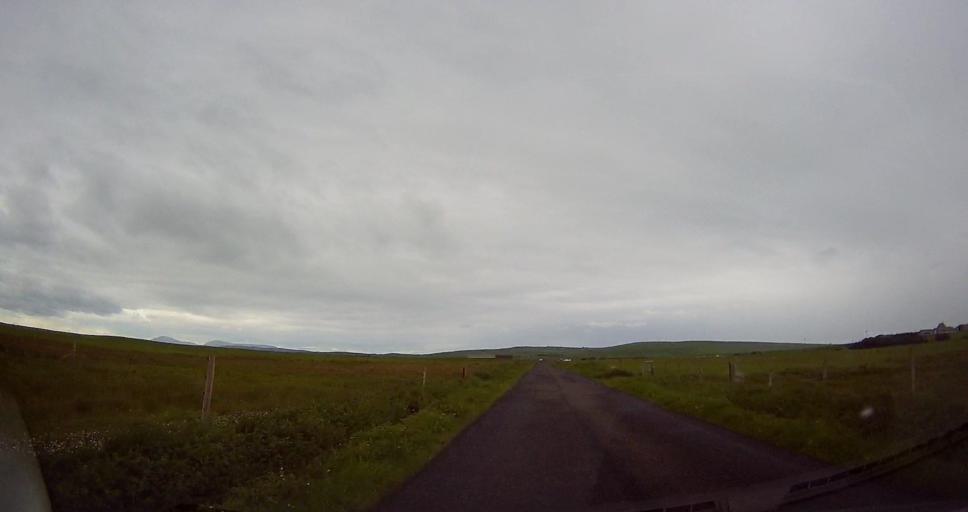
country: GB
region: Scotland
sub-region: Orkney Islands
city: Stromness
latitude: 59.1010
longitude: -3.2629
